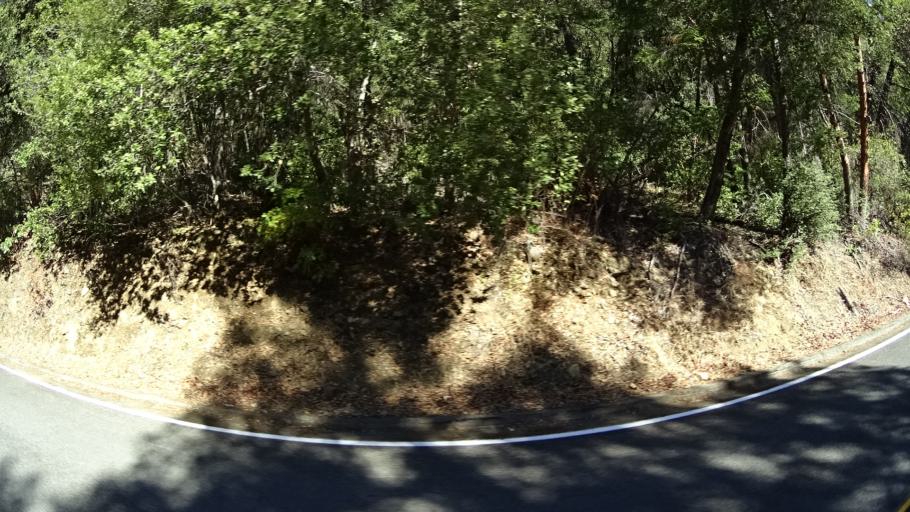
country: US
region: California
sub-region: Siskiyou County
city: Happy Camp
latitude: 41.3776
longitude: -123.4354
